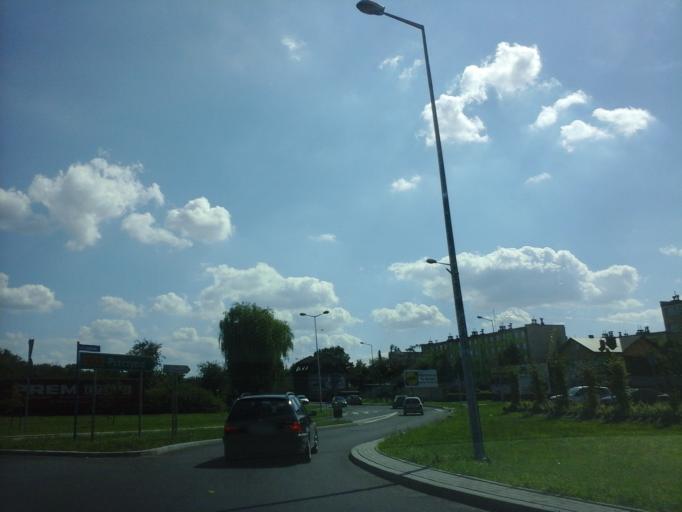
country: PL
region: Lesser Poland Voivodeship
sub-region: Powiat oswiecimski
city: Oswiecim
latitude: 50.0350
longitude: 19.2102
